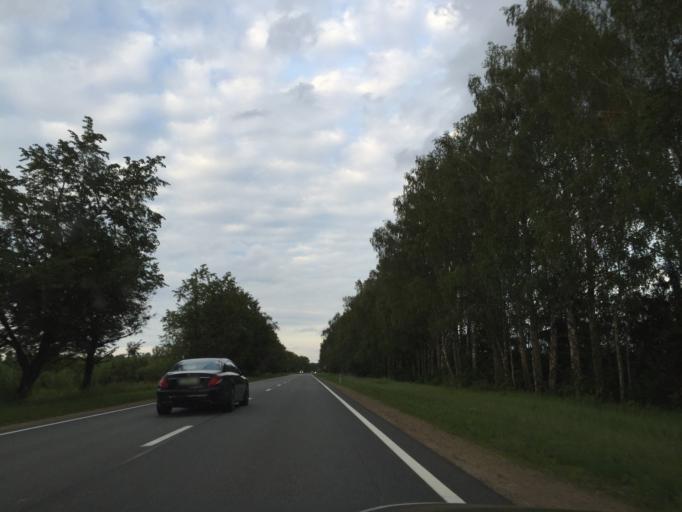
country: LV
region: Babite
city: Pinki
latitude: 56.9206
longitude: 23.8484
